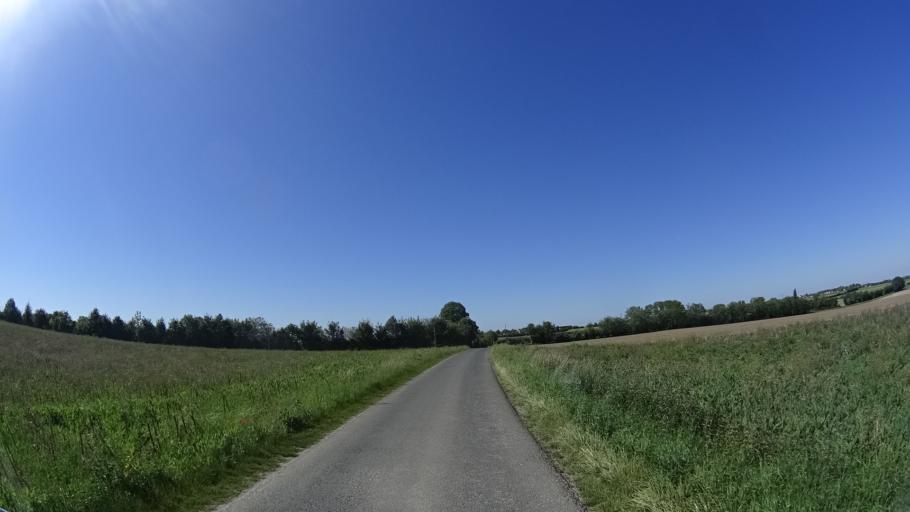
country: FR
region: Pays de la Loire
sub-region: Departement de Maine-et-Loire
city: Doue-la-Fontaine
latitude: 47.2462
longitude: -0.2899
